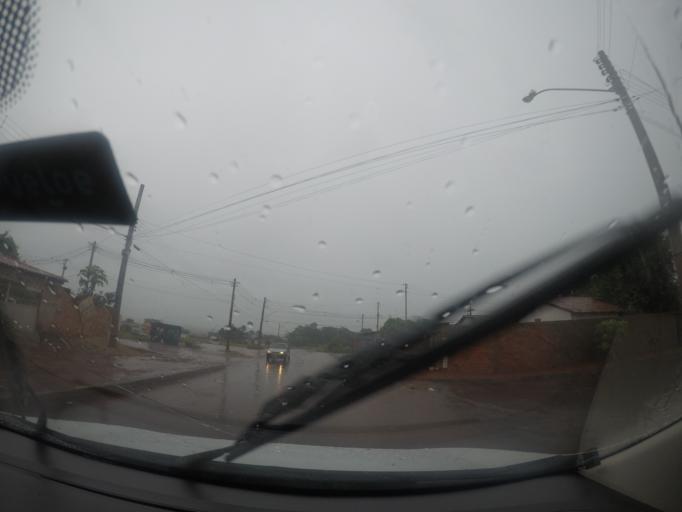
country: BR
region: Goias
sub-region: Goiania
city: Goiania
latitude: -16.5891
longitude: -49.3221
